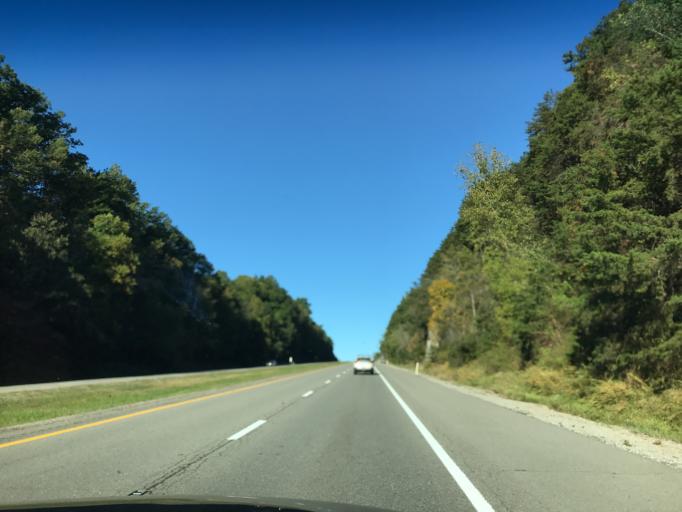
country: US
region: Ohio
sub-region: Washington County
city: Reno
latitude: 39.2503
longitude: -81.3133
